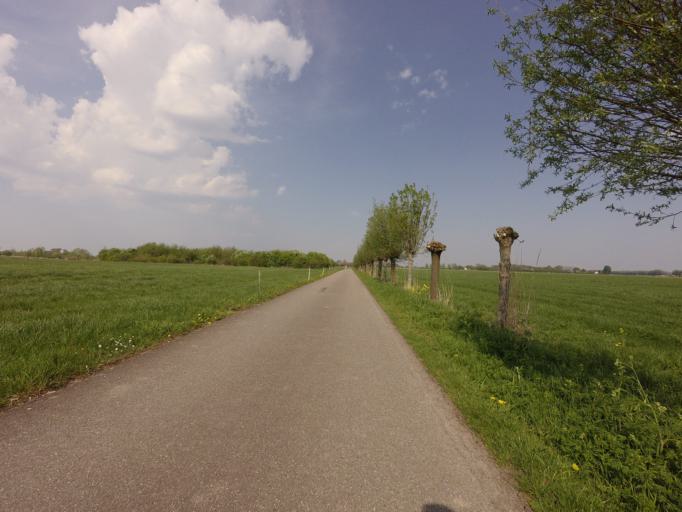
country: NL
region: Utrecht
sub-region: Gemeente Houten
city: Houten
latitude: 52.0196
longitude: 5.1999
